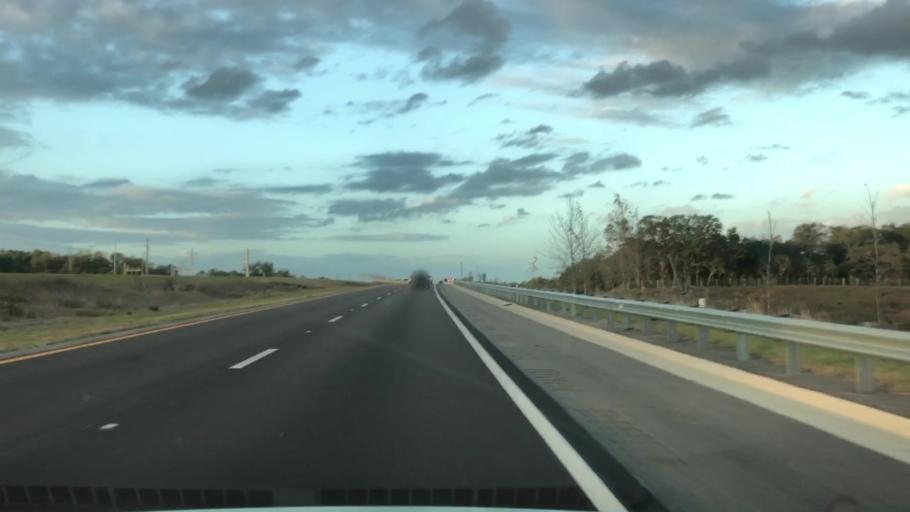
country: US
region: Florida
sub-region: Orange County
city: Zellwood
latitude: 28.7241
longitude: -81.5630
